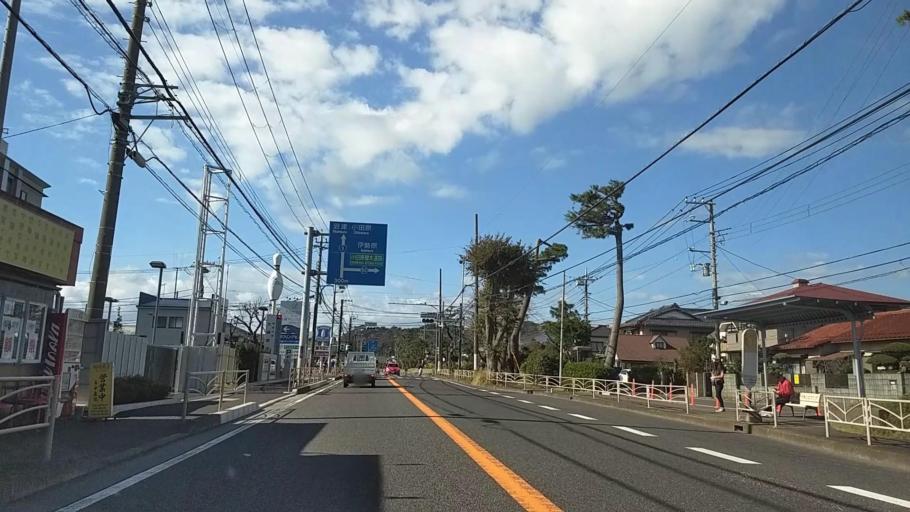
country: JP
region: Kanagawa
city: Oiso
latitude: 35.3045
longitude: 139.2808
